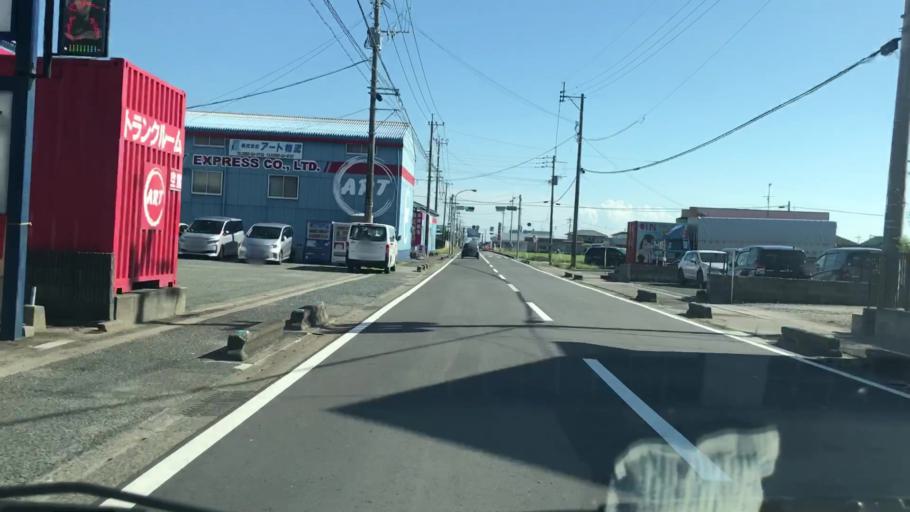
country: JP
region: Saga Prefecture
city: Okawa
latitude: 33.2092
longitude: 130.3354
